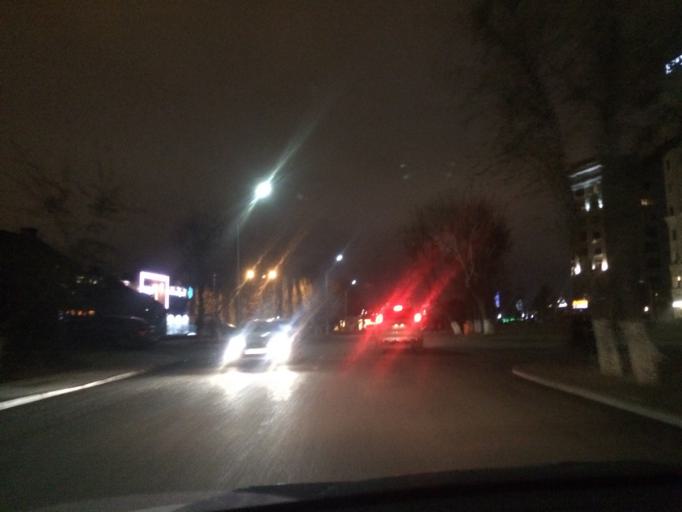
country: KZ
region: Astana Qalasy
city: Astana
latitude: 51.1622
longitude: 71.4179
